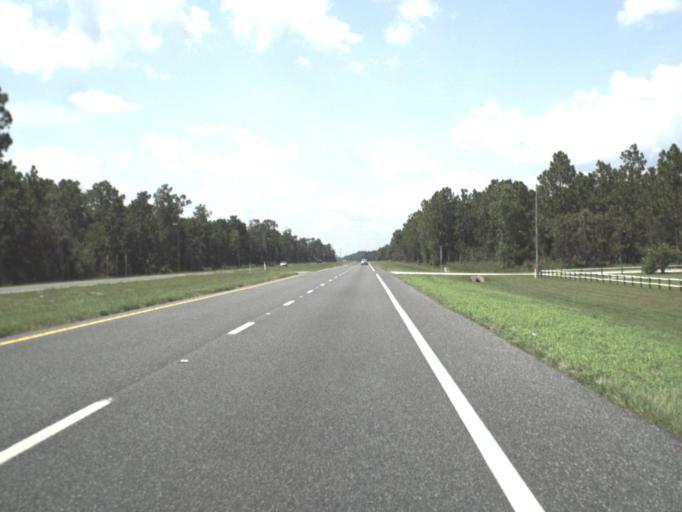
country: US
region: Florida
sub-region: Levy County
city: Inglis
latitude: 29.1186
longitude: -82.6365
